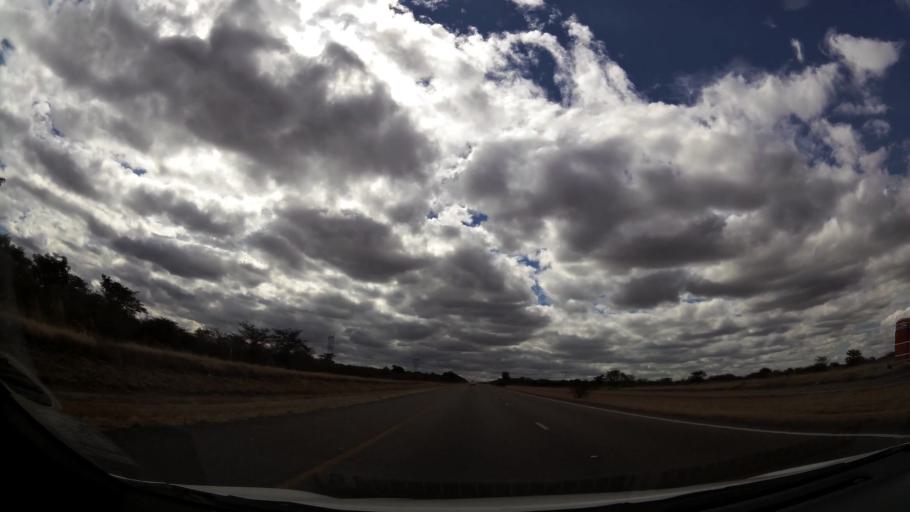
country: ZA
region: Limpopo
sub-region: Waterberg District Municipality
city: Bela-Bela
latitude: -24.8716
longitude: 28.3891
